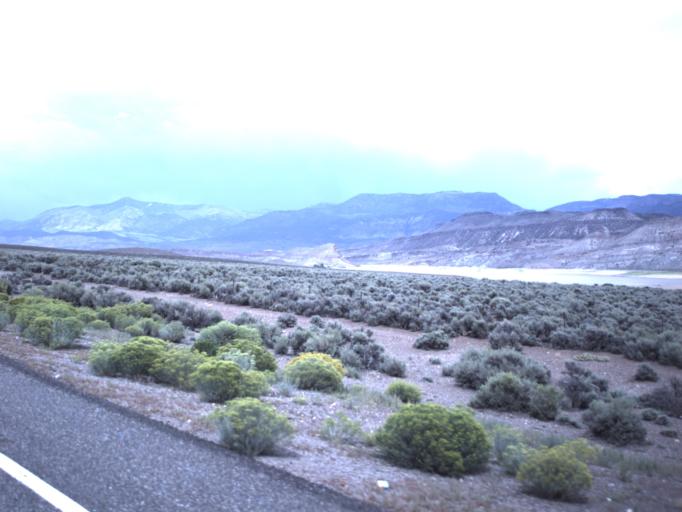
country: US
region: Utah
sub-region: Piute County
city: Junction
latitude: 38.2934
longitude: -112.2253
